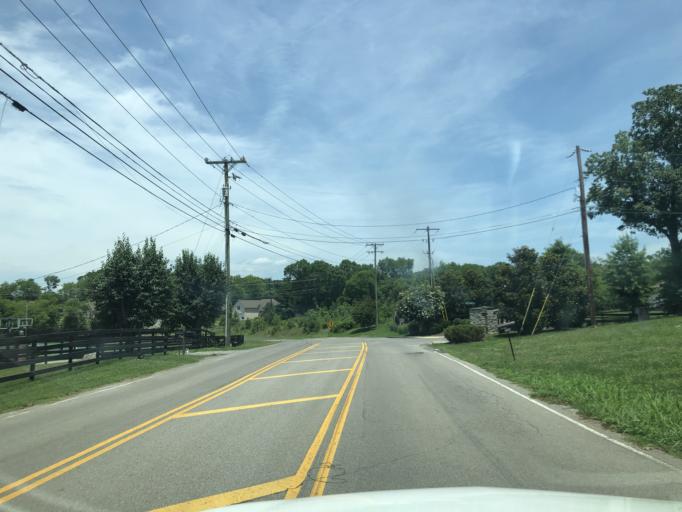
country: US
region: Tennessee
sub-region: Rutherford County
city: La Vergne
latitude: 36.0214
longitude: -86.6432
